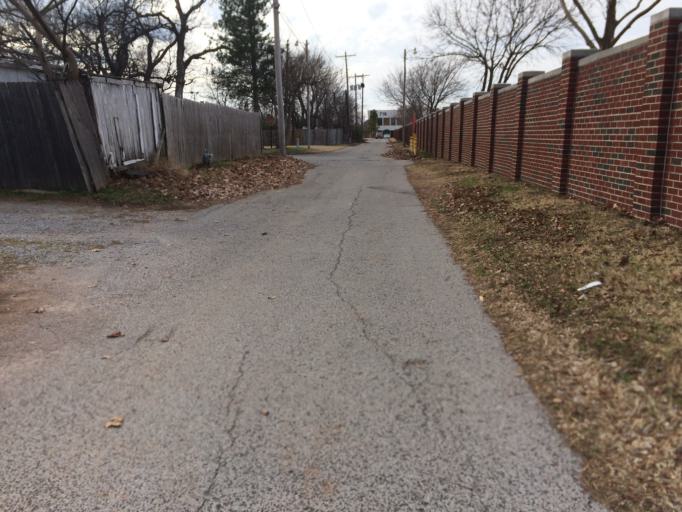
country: US
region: Oklahoma
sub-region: Cleveland County
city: Norman
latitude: 35.2282
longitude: -97.4393
